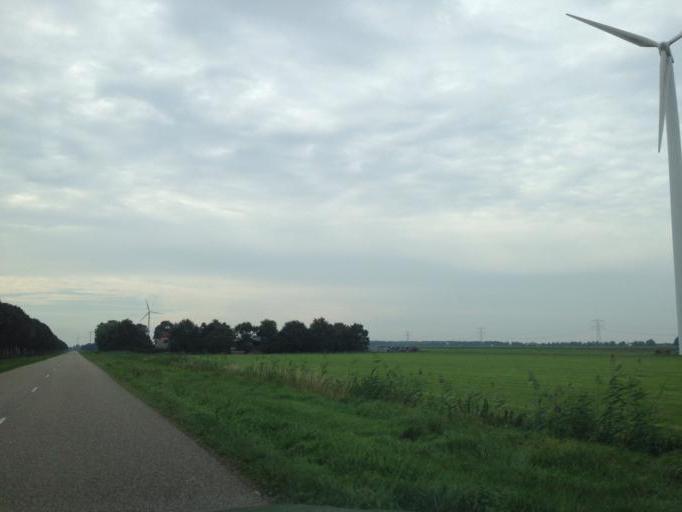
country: NL
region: Flevoland
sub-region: Gemeente Lelystad
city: Lelystad
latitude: 52.4170
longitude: 5.4015
